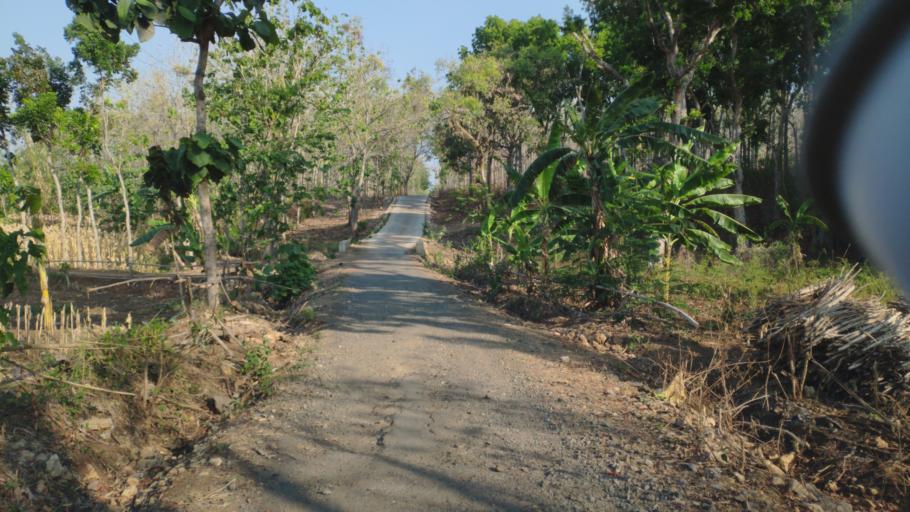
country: ID
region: Central Java
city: Ngapus
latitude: -6.9716
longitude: 111.1831
